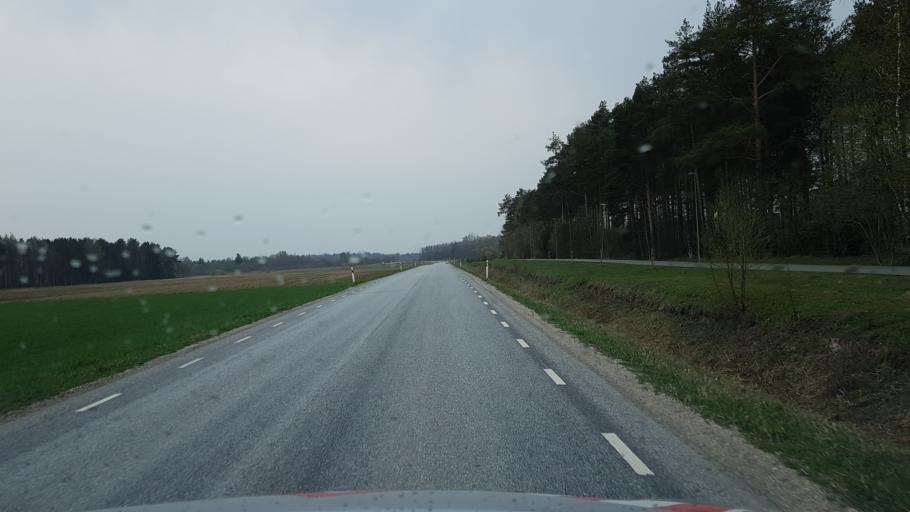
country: EE
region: Harju
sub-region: Saue vald
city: Laagri
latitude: 59.3441
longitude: 24.5944
